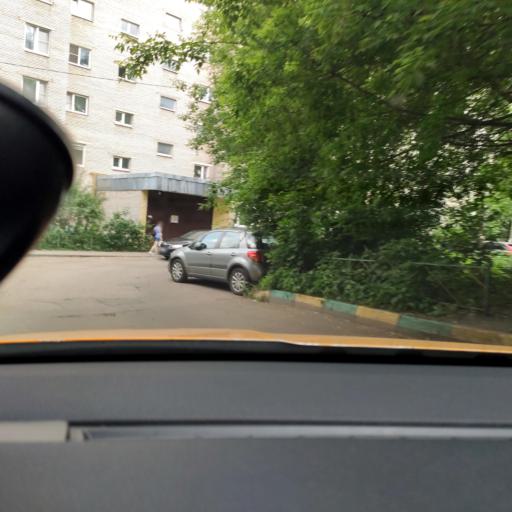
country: RU
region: Moskovskaya
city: Tomilino
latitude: 55.6655
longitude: 37.9595
